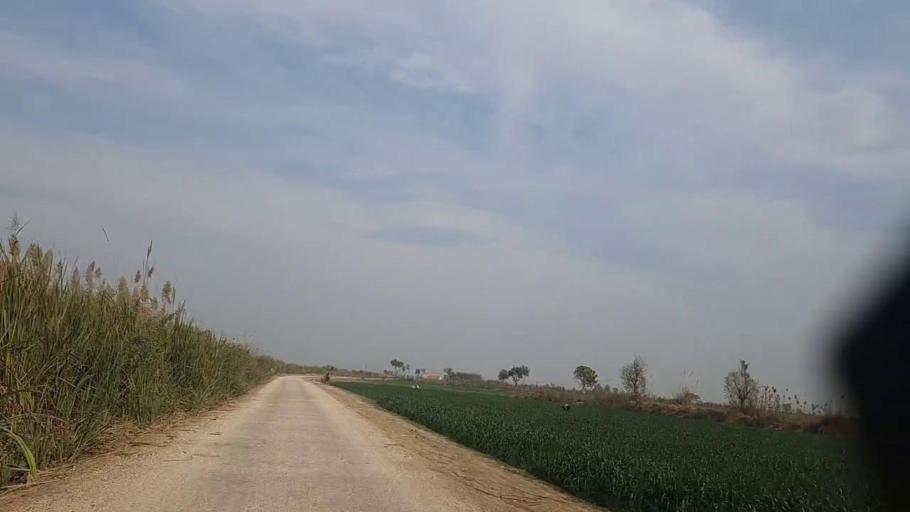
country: PK
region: Sindh
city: Daur
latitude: 26.3760
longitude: 68.2550
